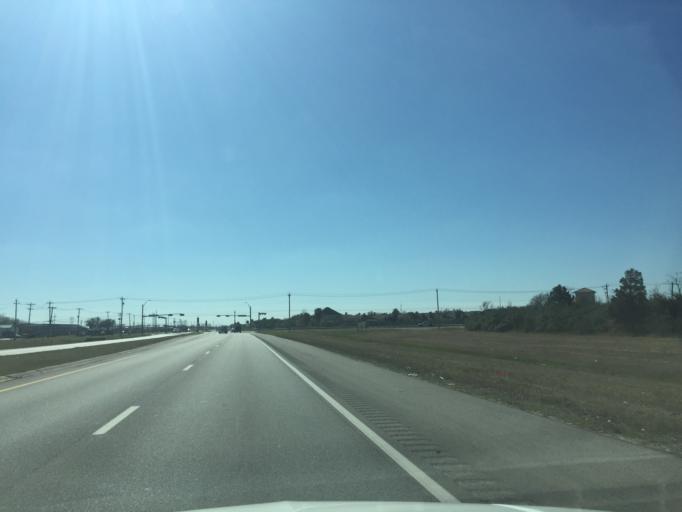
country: US
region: Texas
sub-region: Galveston County
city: Kemah
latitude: 29.5129
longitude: -95.0319
